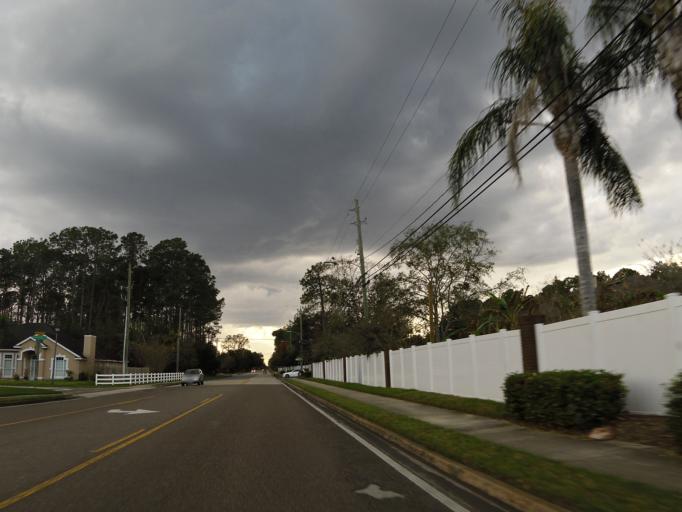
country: US
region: Florida
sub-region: Saint Johns County
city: Fruit Cove
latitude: 30.1725
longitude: -81.5708
